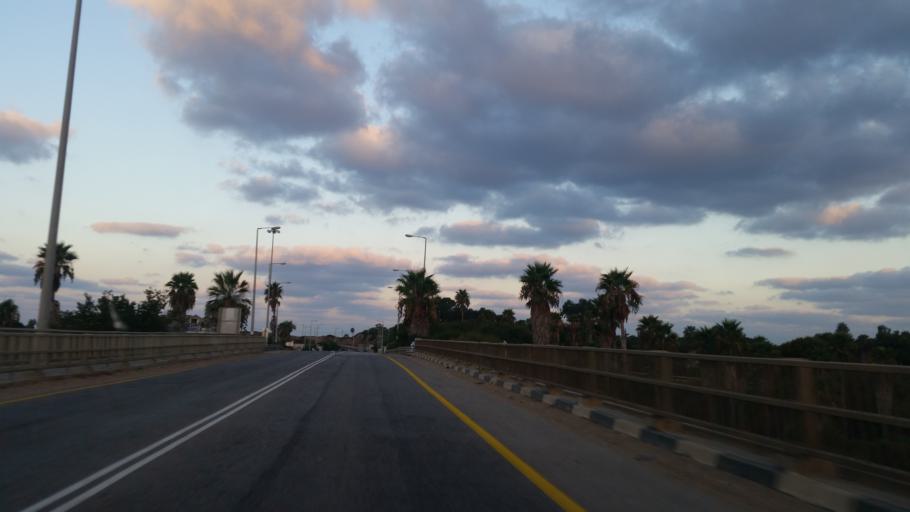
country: IL
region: Haifa
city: `Atlit
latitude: 32.7112
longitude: 34.9519
